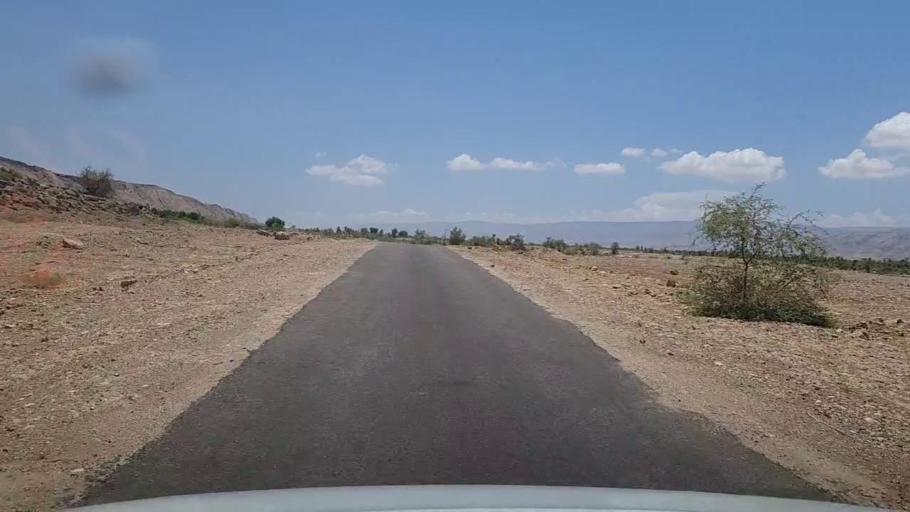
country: PK
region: Sindh
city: Bhan
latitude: 26.2865
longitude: 67.5329
